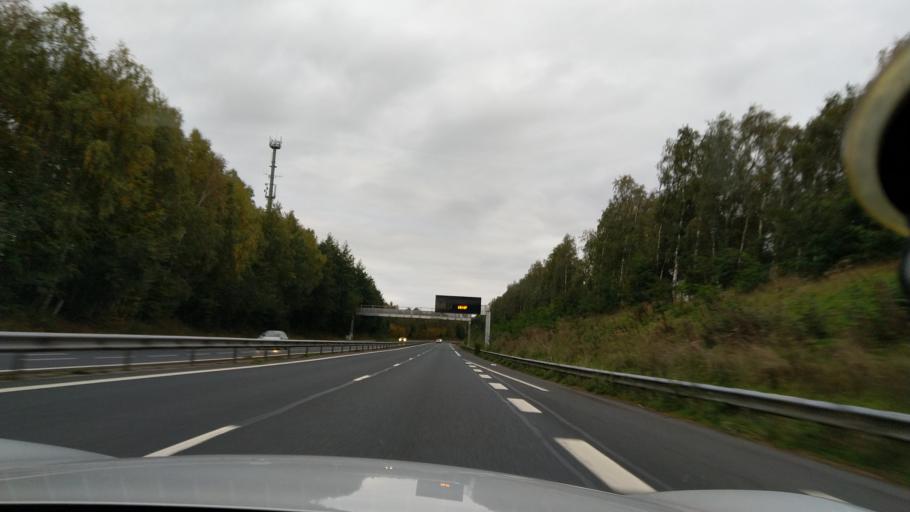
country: FR
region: Haute-Normandie
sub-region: Departement de la Seine-Maritime
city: Saint-Martin-Osmonville
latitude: 49.6441
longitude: 1.2662
